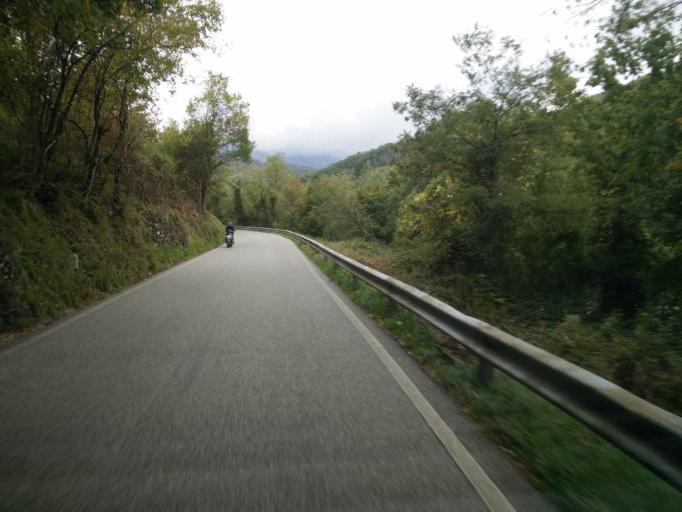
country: IT
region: Tuscany
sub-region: Provincia di Massa-Carrara
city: Casola in Lunigiana
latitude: 44.1900
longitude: 10.1340
